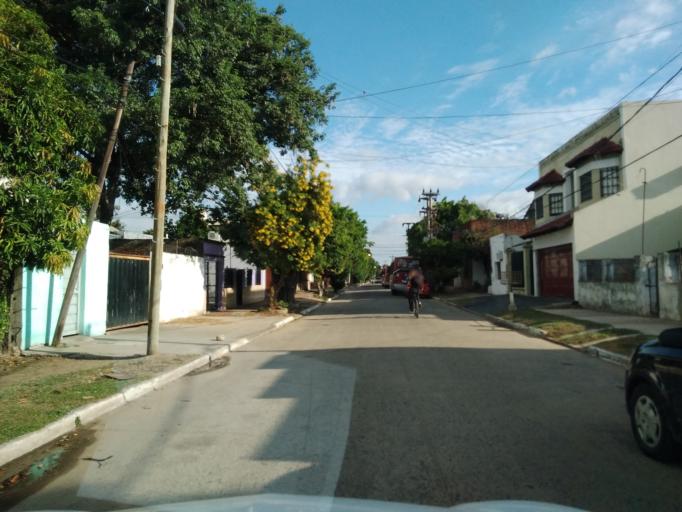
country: AR
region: Corrientes
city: Corrientes
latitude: -27.4626
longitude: -58.8193
